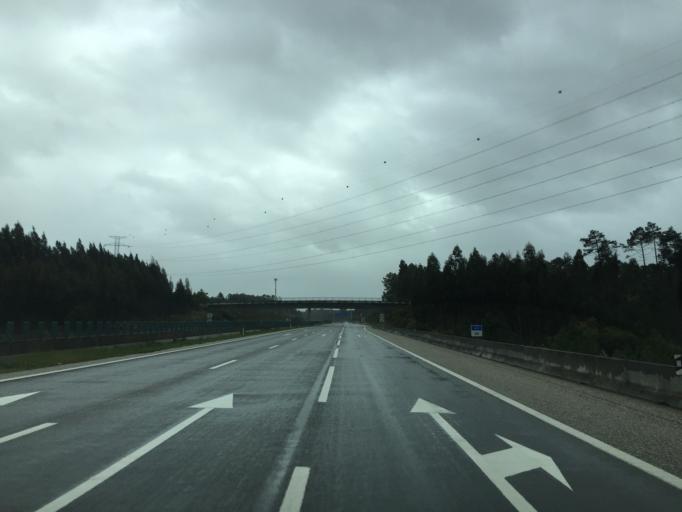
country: PT
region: Leiria
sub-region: Leiria
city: Monte Redondo
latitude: 39.9129
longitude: -8.7995
